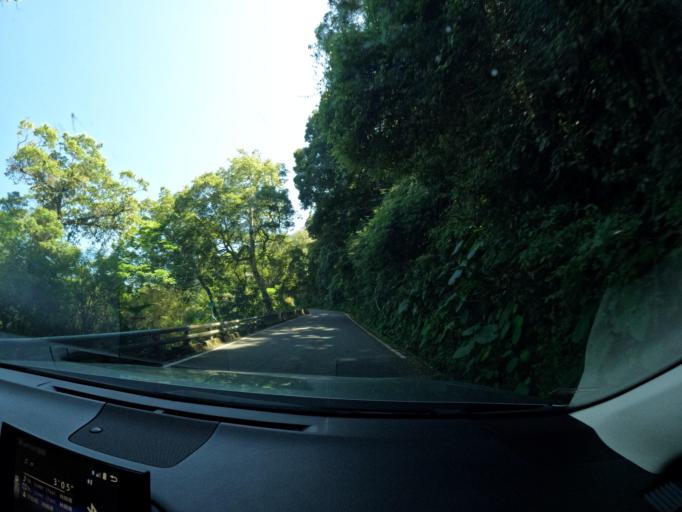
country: TW
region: Taiwan
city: Yujing
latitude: 23.2838
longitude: 120.8650
